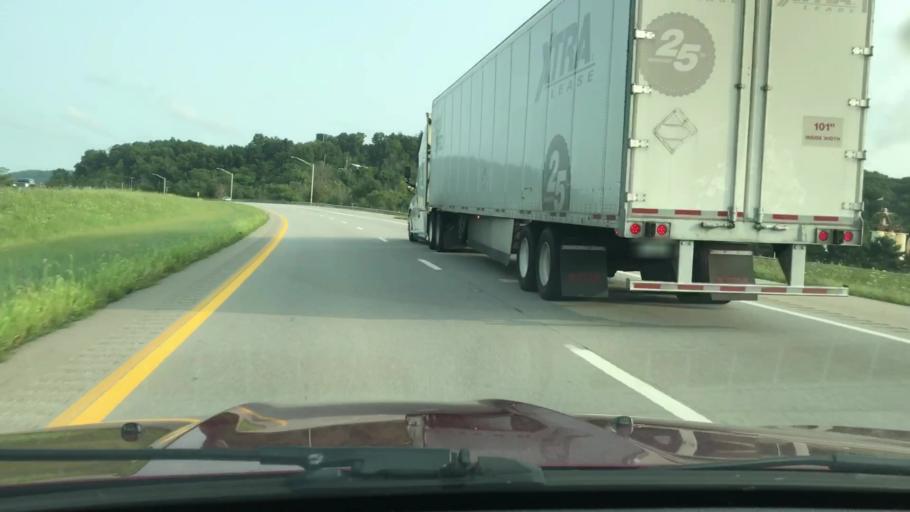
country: US
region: Ohio
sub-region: Guernsey County
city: Byesville
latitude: 39.9681
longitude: -81.5298
